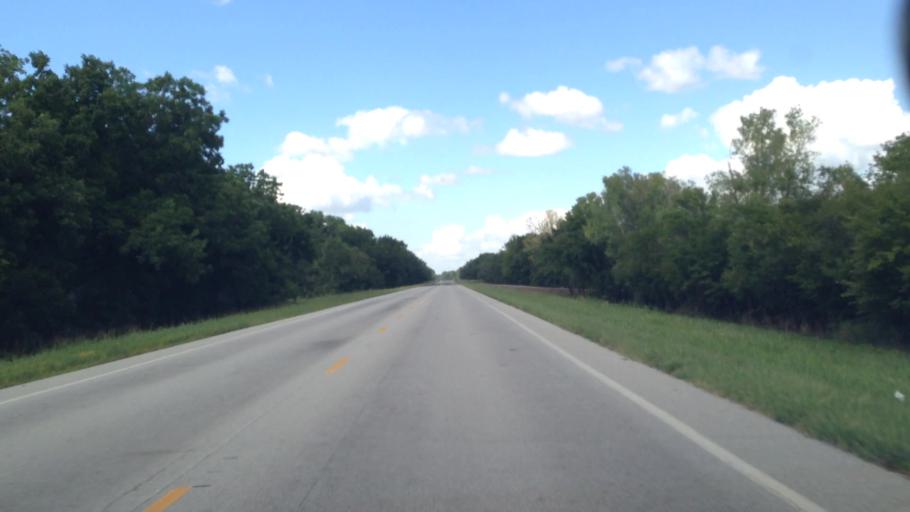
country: US
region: Kansas
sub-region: Labette County
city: Chetopa
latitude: 37.0679
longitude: -95.1028
